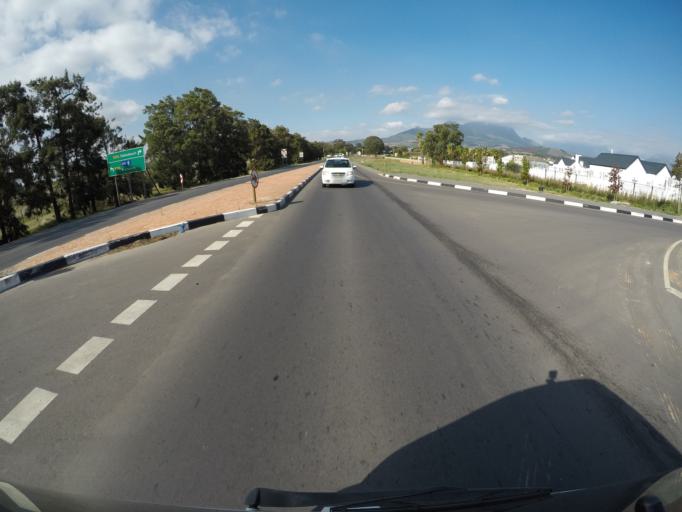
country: ZA
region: Western Cape
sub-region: Cape Winelands District Municipality
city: Stellenbosch
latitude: -33.8758
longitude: 18.8112
